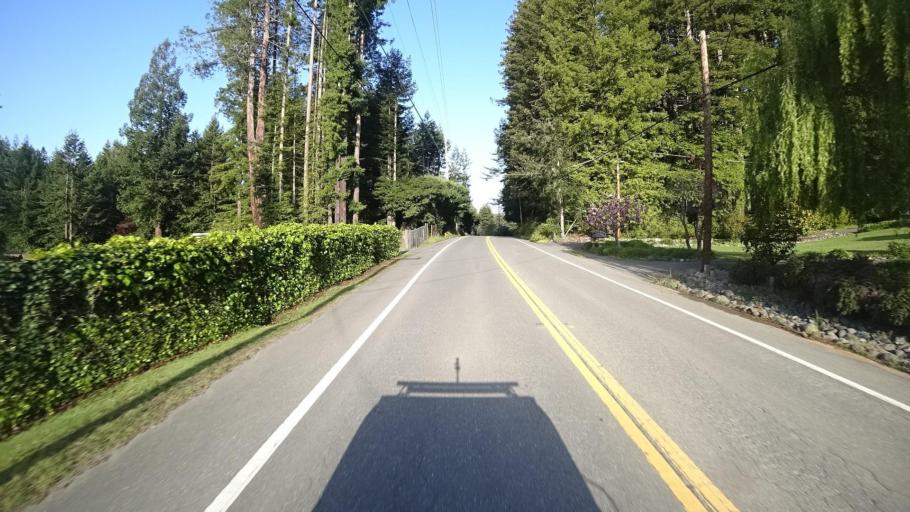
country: US
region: California
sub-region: Humboldt County
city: Myrtletown
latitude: 40.7603
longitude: -124.0567
